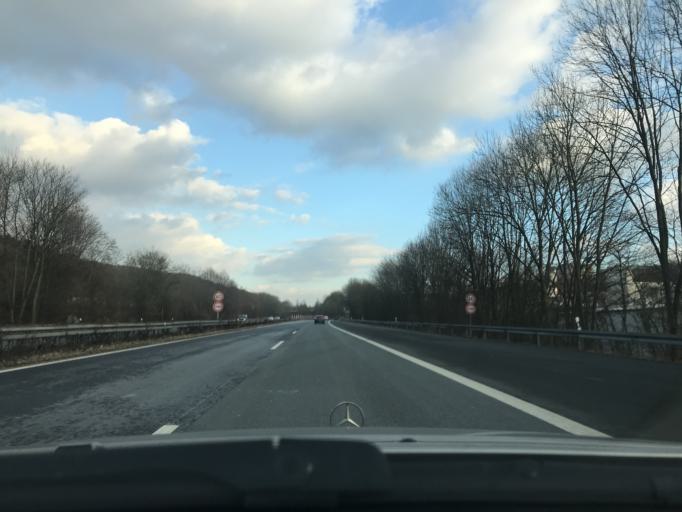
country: DE
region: North Rhine-Westphalia
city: Iserlohn
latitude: 51.3877
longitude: 7.7238
